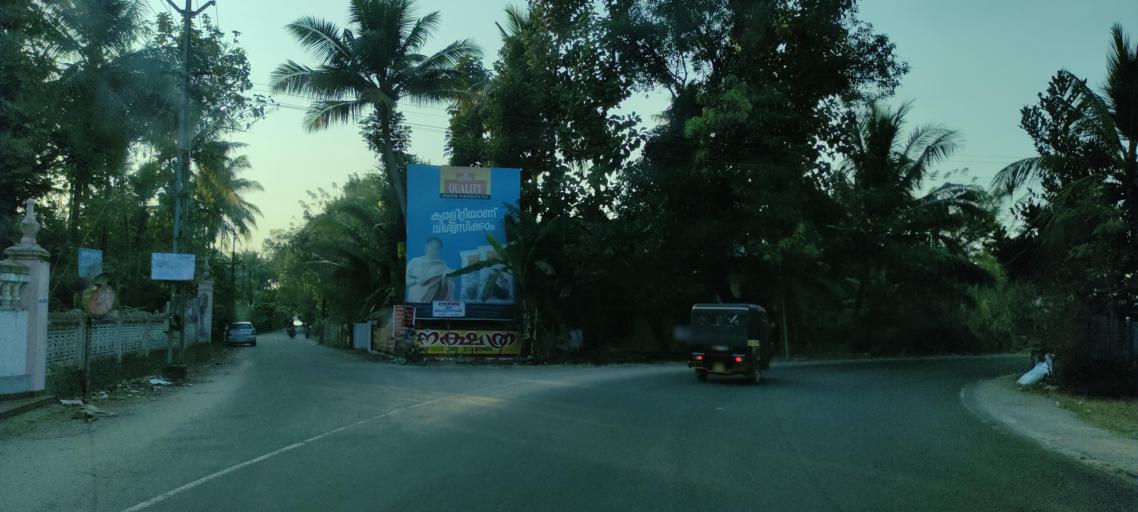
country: IN
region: Kerala
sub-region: Alappuzha
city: Kutiatodu
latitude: 9.7747
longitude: 76.3382
